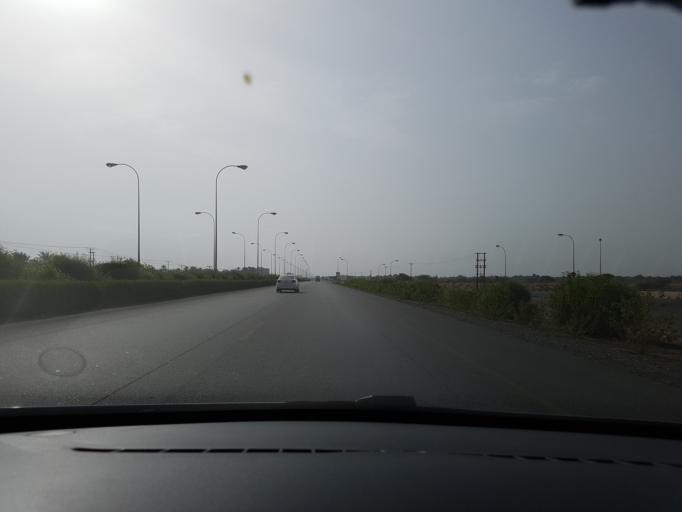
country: OM
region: Al Batinah
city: Al Sohar
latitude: 24.4094
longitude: 56.6466
